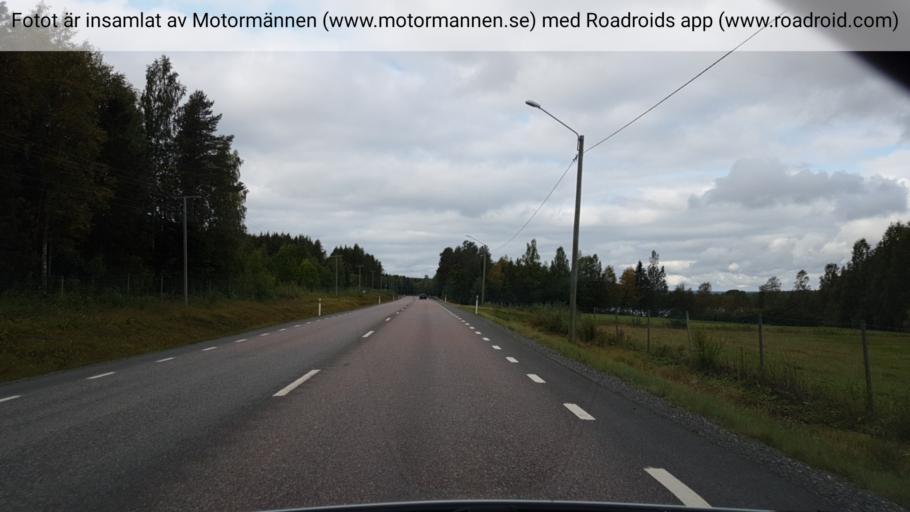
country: SE
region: Vaesterbotten
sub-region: Skelleftea Kommun
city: Forsbacka
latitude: 64.8076
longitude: 20.6746
